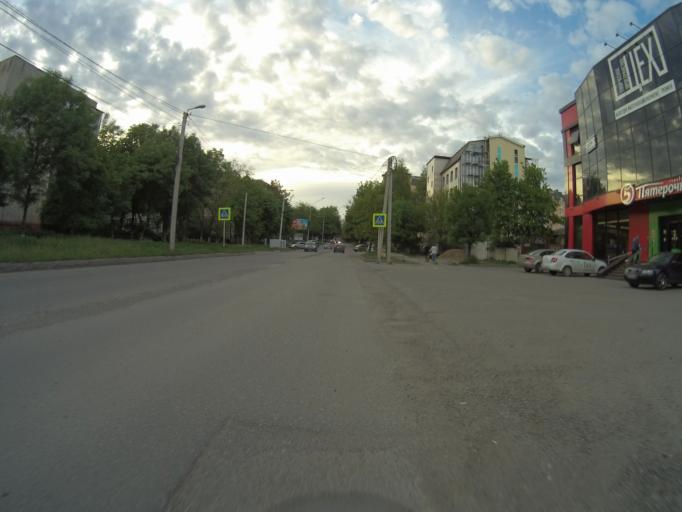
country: RU
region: Stavropol'skiy
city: Yessentukskaya
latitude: 44.0479
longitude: 42.8964
